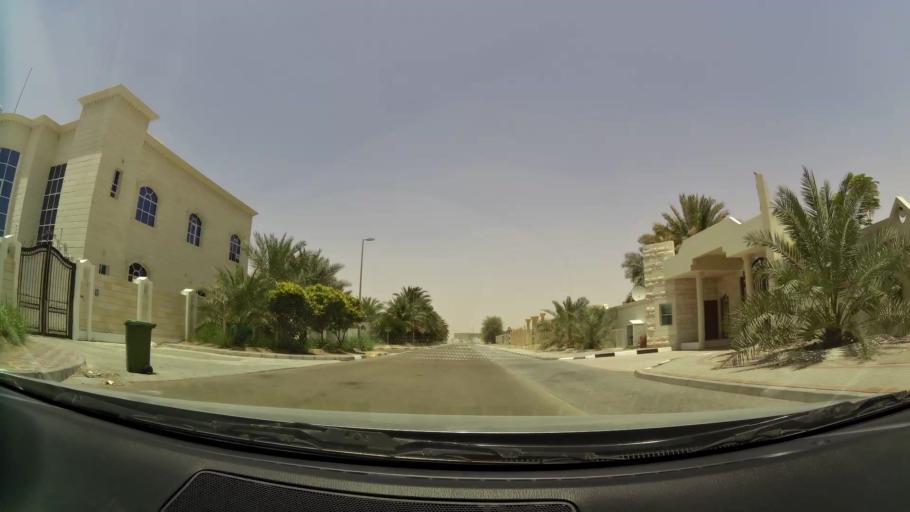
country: OM
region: Al Buraimi
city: Al Buraymi
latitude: 24.2901
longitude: 55.7396
